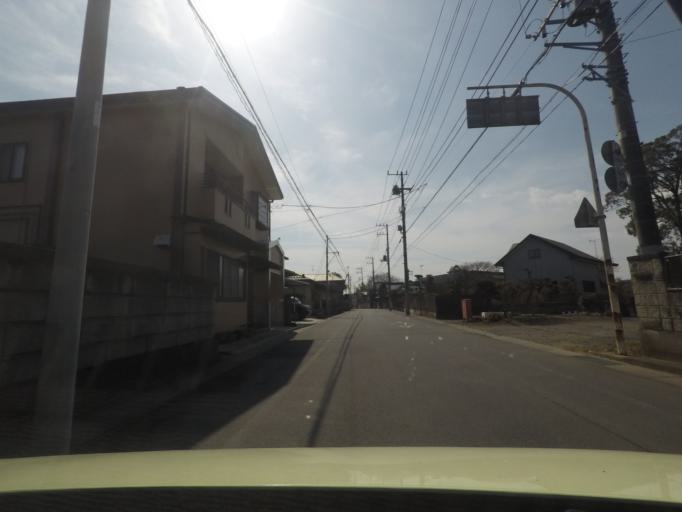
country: JP
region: Ibaraki
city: Ishioka
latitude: 36.1782
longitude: 140.3607
